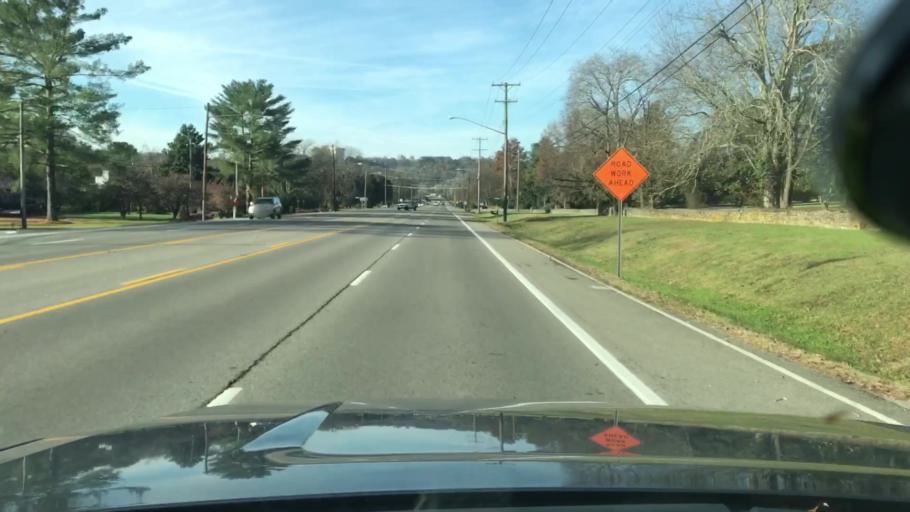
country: US
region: Tennessee
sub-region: Davidson County
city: Belle Meade
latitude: 36.0952
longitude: -86.8801
